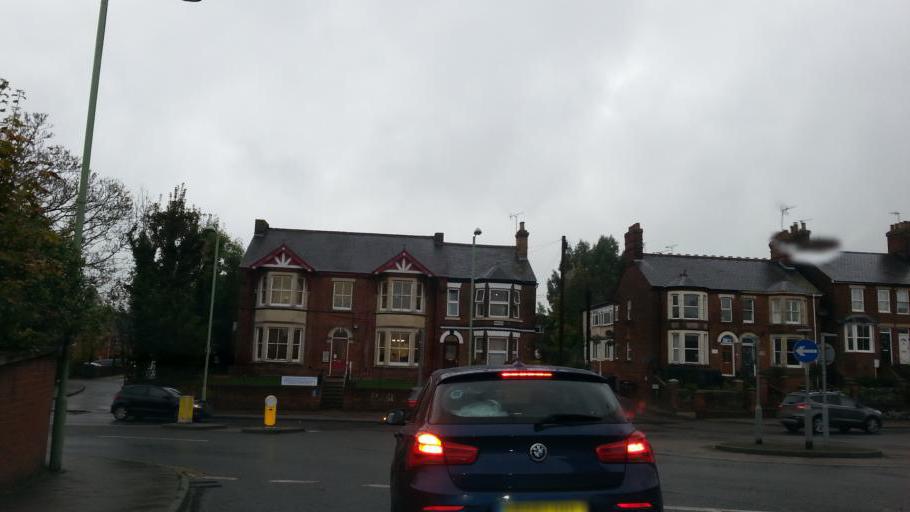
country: GB
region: England
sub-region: Suffolk
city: Haverhill
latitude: 52.0851
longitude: 0.4378
